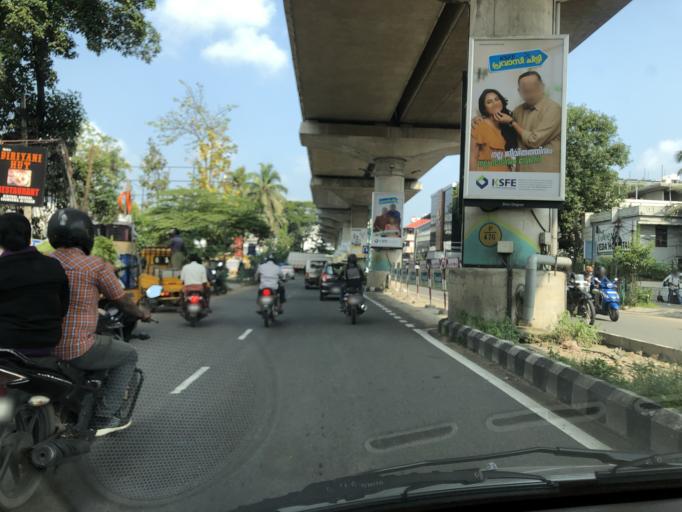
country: IN
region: Kerala
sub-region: Ernakulam
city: Elur
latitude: 10.0124
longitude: 76.3029
